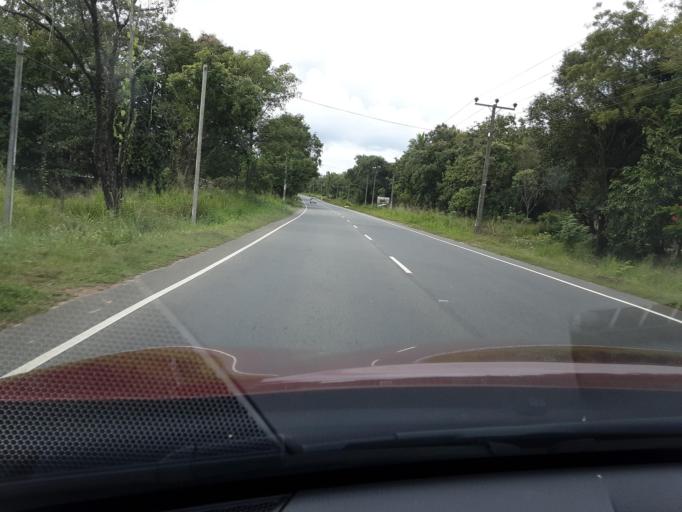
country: LK
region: Uva
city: Badulla
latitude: 7.3952
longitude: 81.1256
